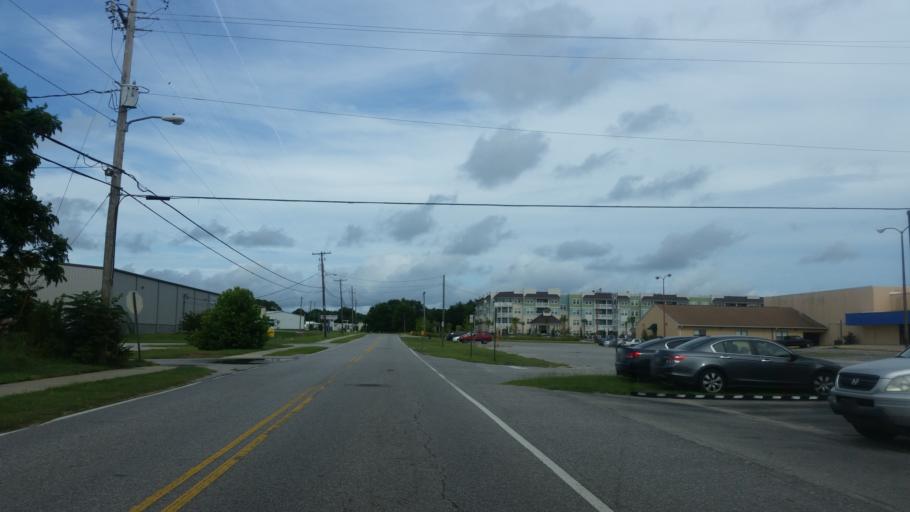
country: US
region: Florida
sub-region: Escambia County
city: Goulding
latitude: 30.4487
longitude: -87.2349
